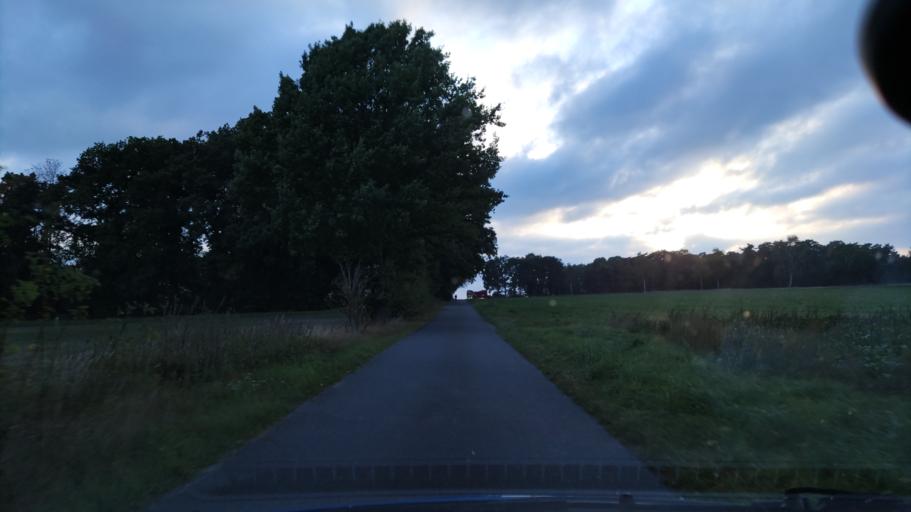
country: DE
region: Lower Saxony
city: Tosterglope
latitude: 53.2162
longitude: 10.8194
